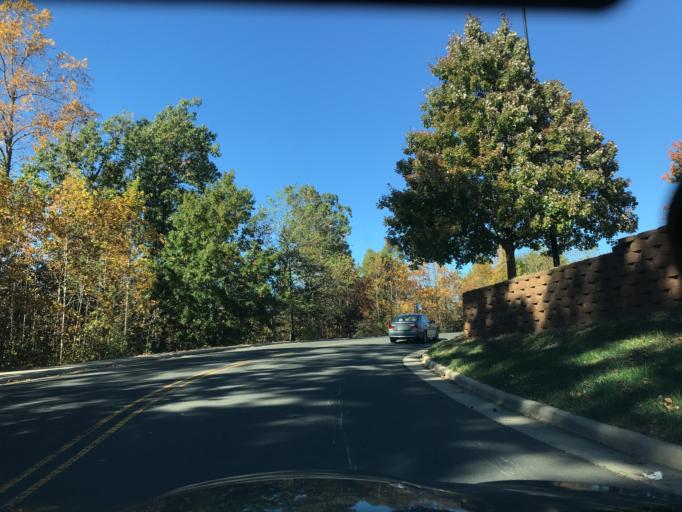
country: US
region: North Carolina
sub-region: Wake County
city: Morrisville
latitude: 35.9009
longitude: -78.7883
